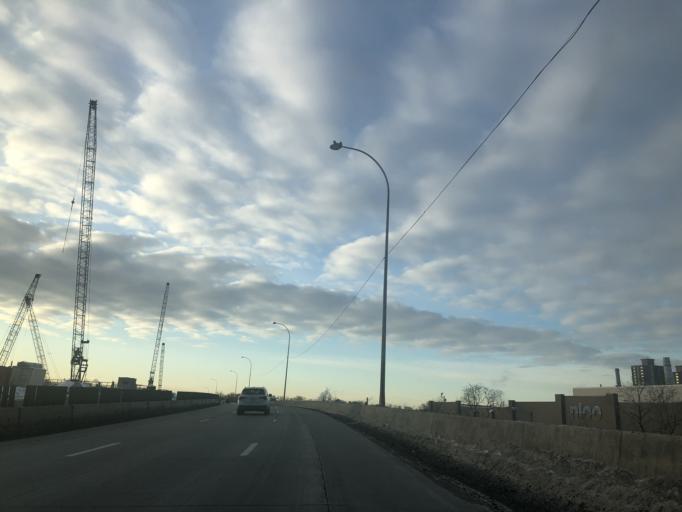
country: US
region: Minnesota
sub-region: Hennepin County
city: Minneapolis
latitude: 44.9505
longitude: -93.2755
